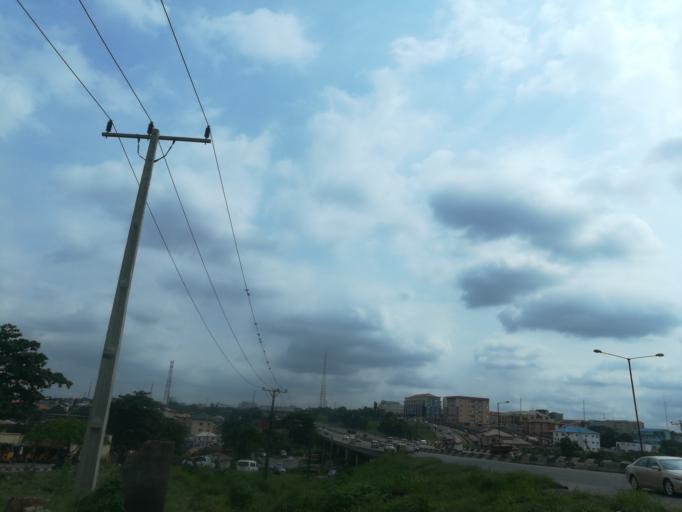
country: NG
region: Lagos
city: Ikeja
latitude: 6.6306
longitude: 3.3651
